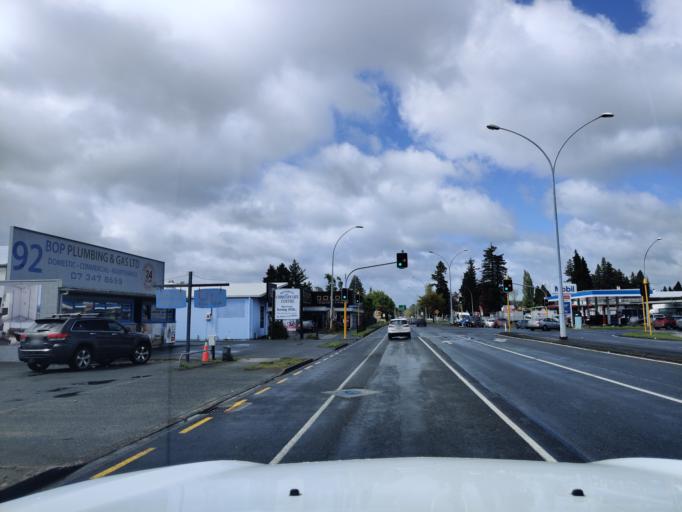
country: NZ
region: Bay of Plenty
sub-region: Rotorua District
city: Rotorua
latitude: -38.1329
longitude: 176.2342
